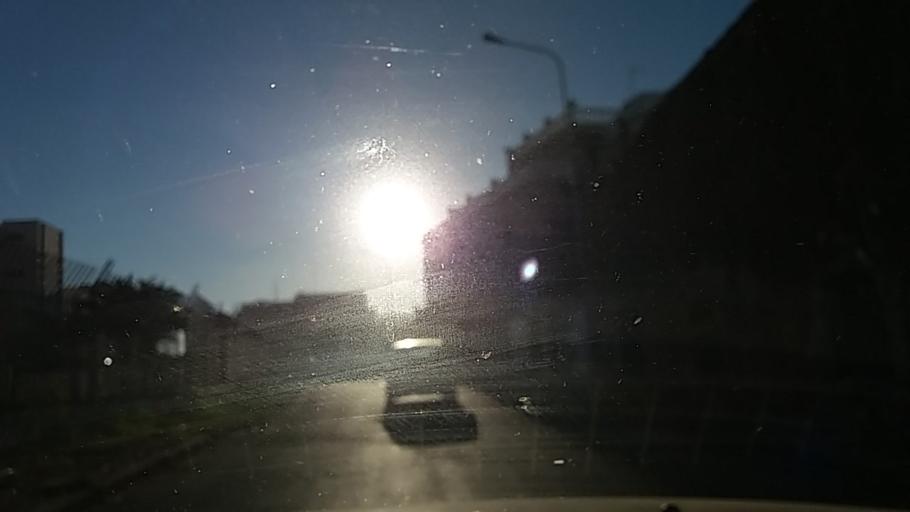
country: MA
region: Tanger-Tetouan
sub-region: Tanger-Assilah
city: Tangier
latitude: 35.7836
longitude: -5.8245
